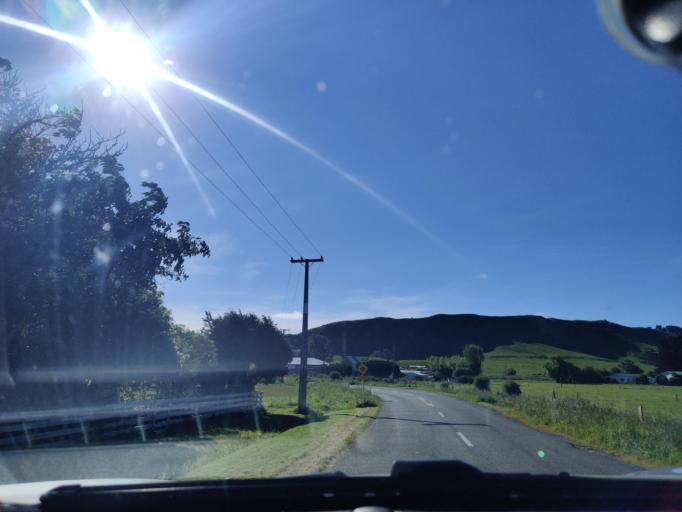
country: NZ
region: Manawatu-Wanganui
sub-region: Palmerston North City
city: Palmerston North
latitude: -40.5155
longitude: 175.7497
